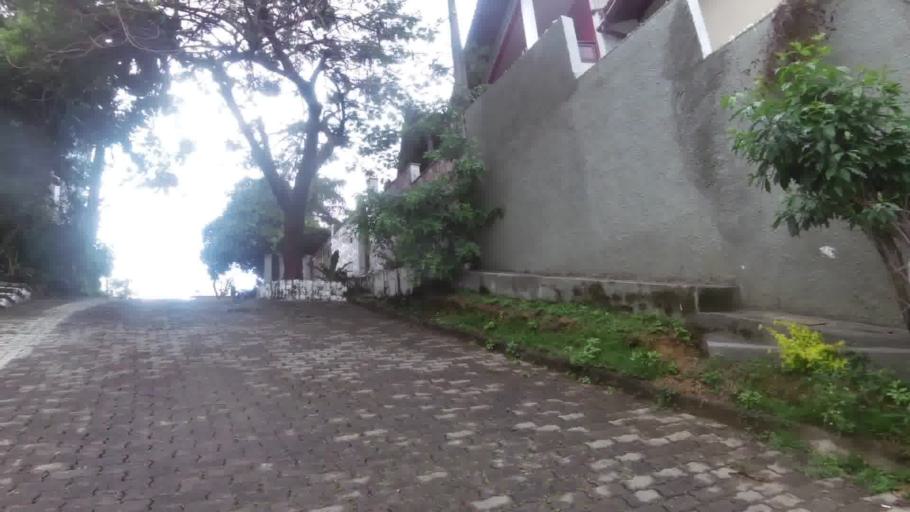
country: BR
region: Espirito Santo
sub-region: Piuma
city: Piuma
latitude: -20.8346
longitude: -40.6953
